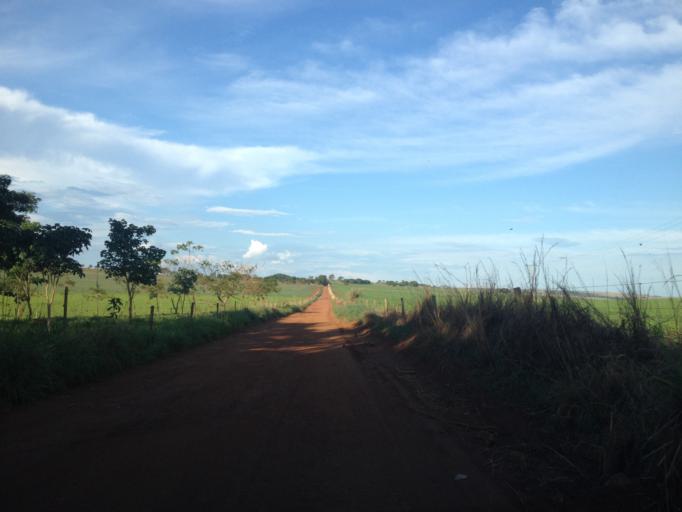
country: BR
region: Goias
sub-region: Abadiania
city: Abadiania
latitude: -15.9973
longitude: -48.5436
